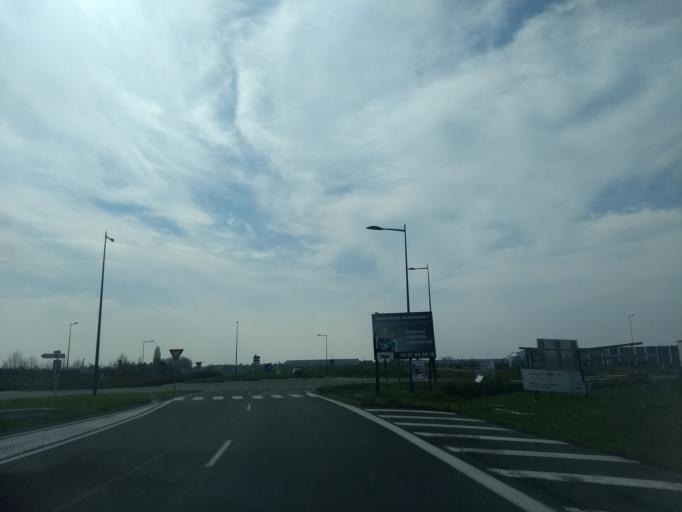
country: FR
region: Nord-Pas-de-Calais
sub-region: Departement du Nord
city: Courchelettes
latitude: 50.3521
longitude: 3.0392
